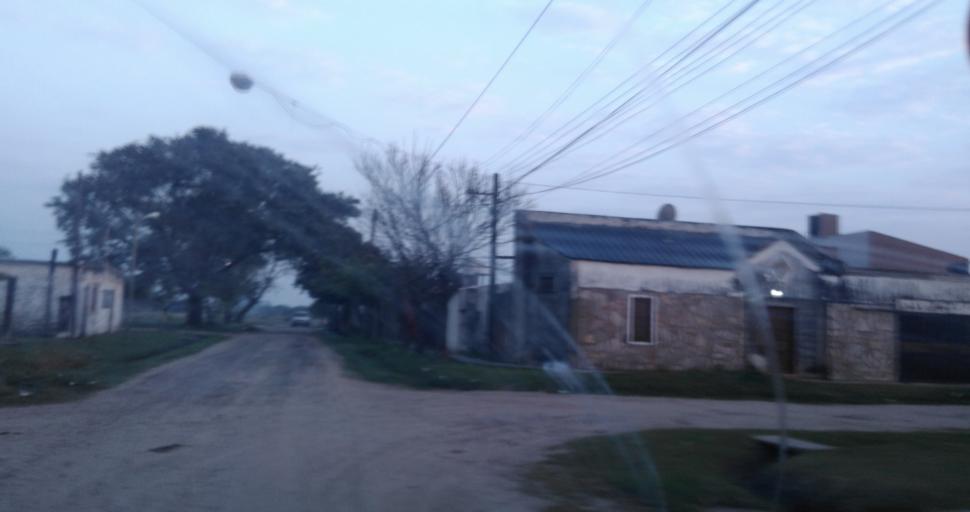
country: AR
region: Chaco
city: Fontana
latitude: -27.4477
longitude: -59.0377
